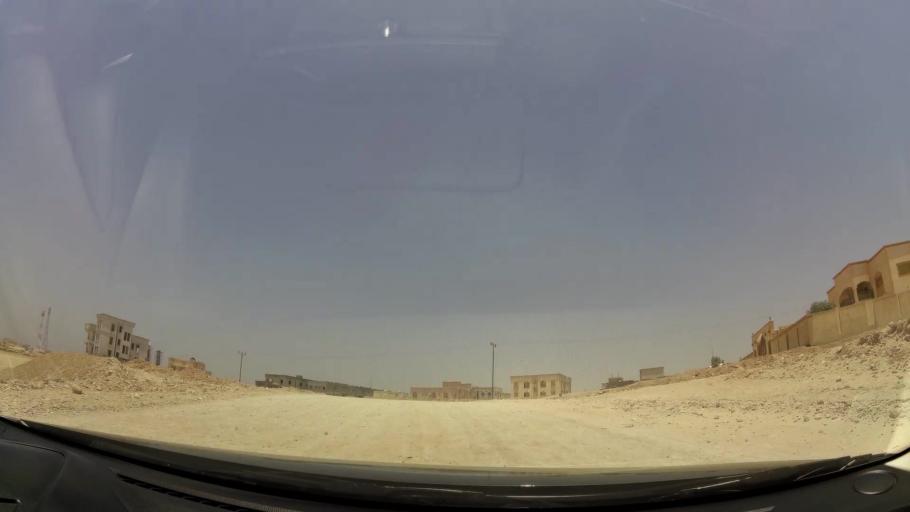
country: OM
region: Zufar
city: Salalah
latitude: 17.0891
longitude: 54.1622
